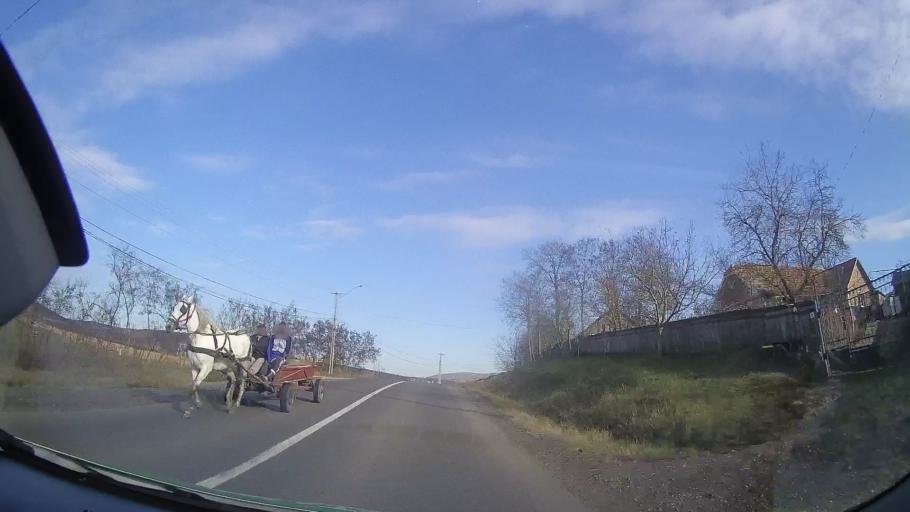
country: RO
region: Mures
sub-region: Comuna Valea Larga
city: Valea Larga
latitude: 46.5863
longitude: 24.0959
